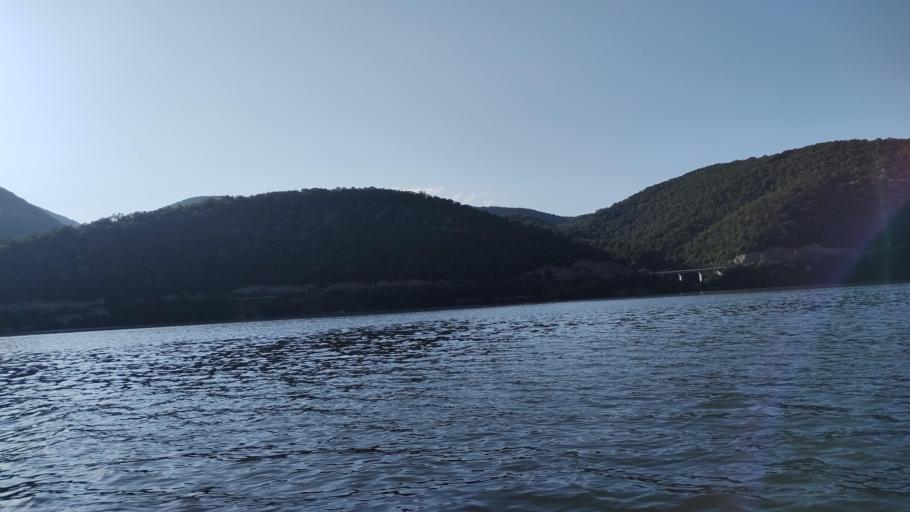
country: RO
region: Mehedinti
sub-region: Comuna Dubova
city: Dubova
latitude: 44.5804
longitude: 22.2487
